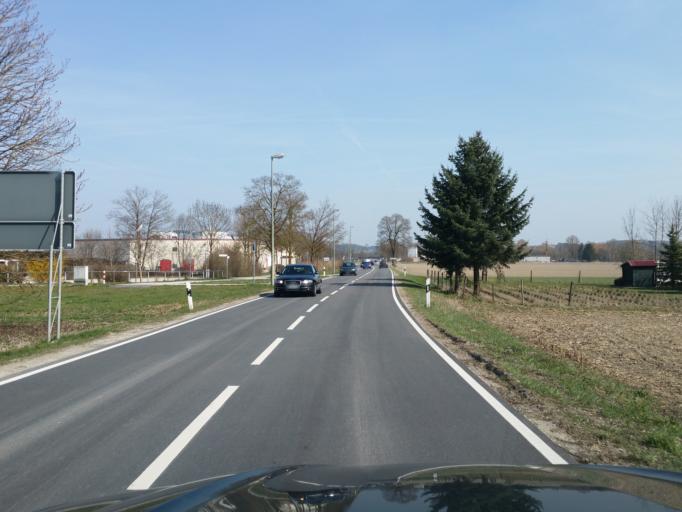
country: DE
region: Bavaria
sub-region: Upper Bavaria
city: Moosburg
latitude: 48.4650
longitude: 11.9593
